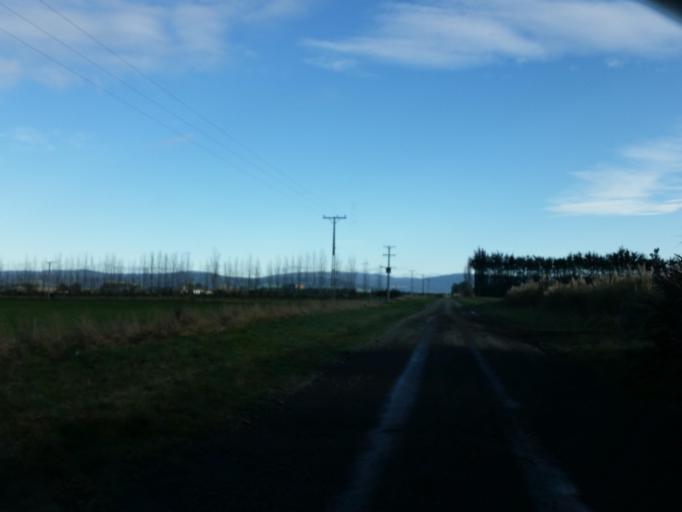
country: NZ
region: Southland
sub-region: Southland District
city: Winton
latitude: -46.1393
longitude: 168.1247
